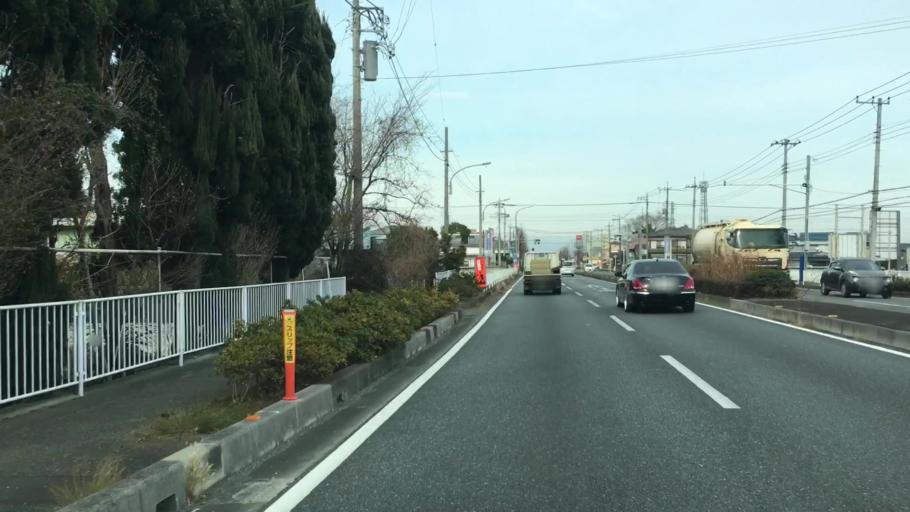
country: JP
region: Saitama
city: Kumagaya
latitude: 36.1630
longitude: 139.3707
